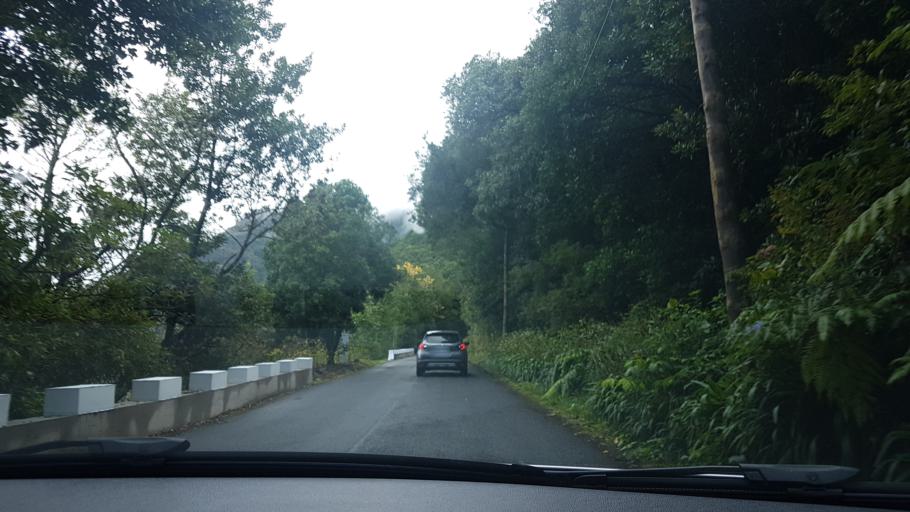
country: PT
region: Madeira
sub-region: Sao Vicente
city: Sao Vicente
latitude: 32.7627
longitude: -17.0217
